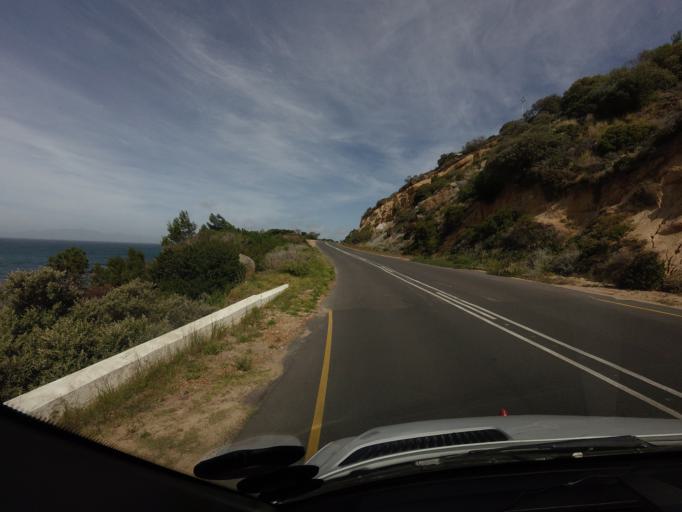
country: ZA
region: Western Cape
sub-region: City of Cape Town
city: Retreat
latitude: -34.2247
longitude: 18.4670
